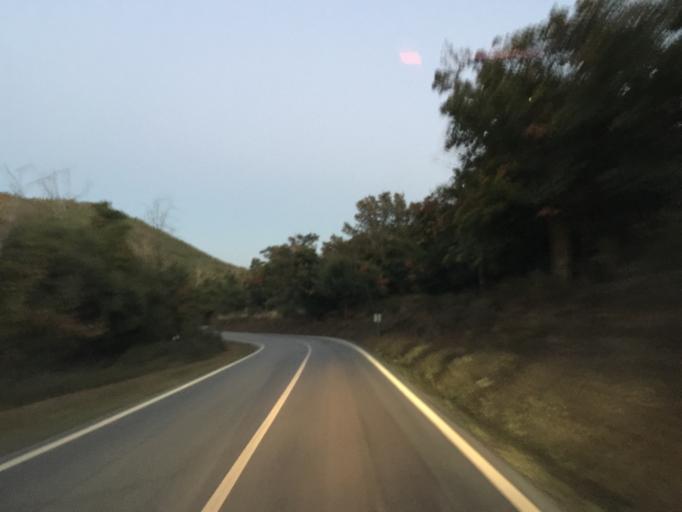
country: PT
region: Portalegre
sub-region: Castelo de Vide
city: Castelo de Vide
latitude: 39.4014
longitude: -7.4345
